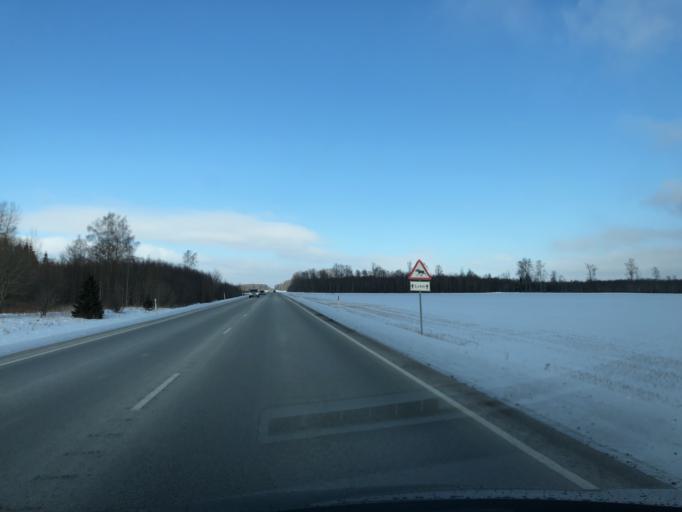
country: EE
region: Jaervamaa
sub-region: Paide linn
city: Paide
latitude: 58.7895
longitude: 25.7582
